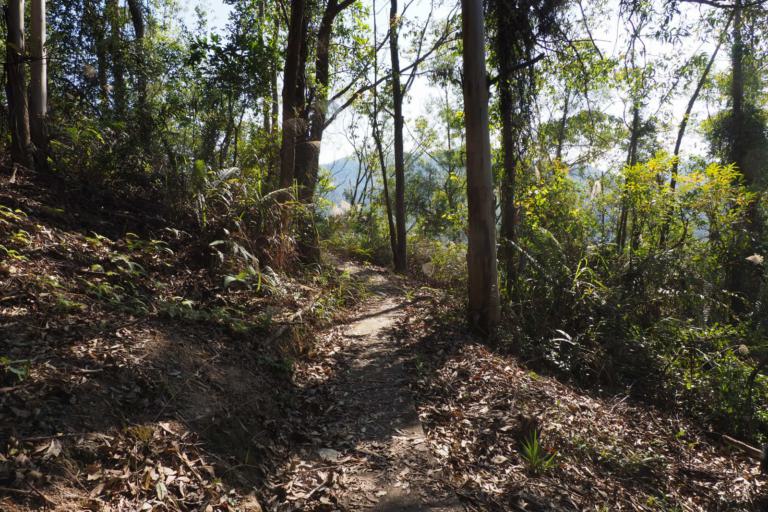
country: CN
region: Guangdong
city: Huancheng
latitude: 22.4652
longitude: 113.4086
